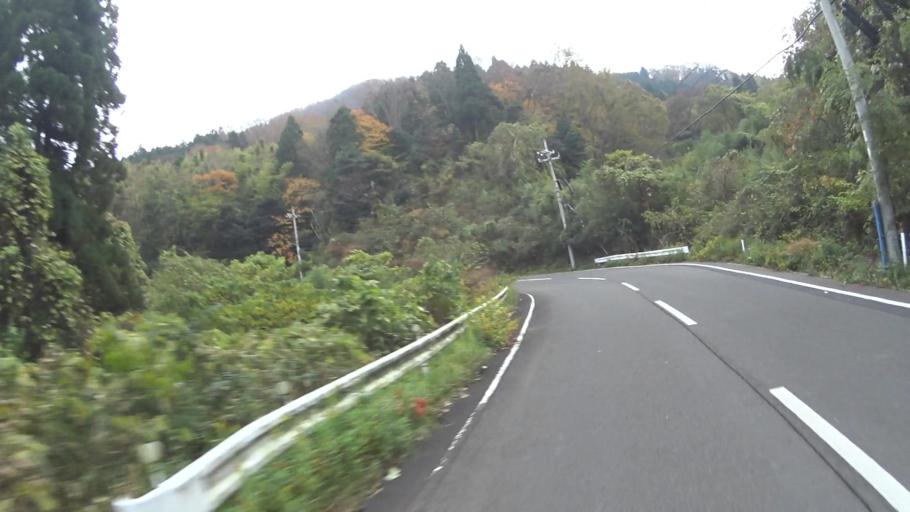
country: JP
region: Kyoto
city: Maizuru
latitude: 35.5544
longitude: 135.4541
